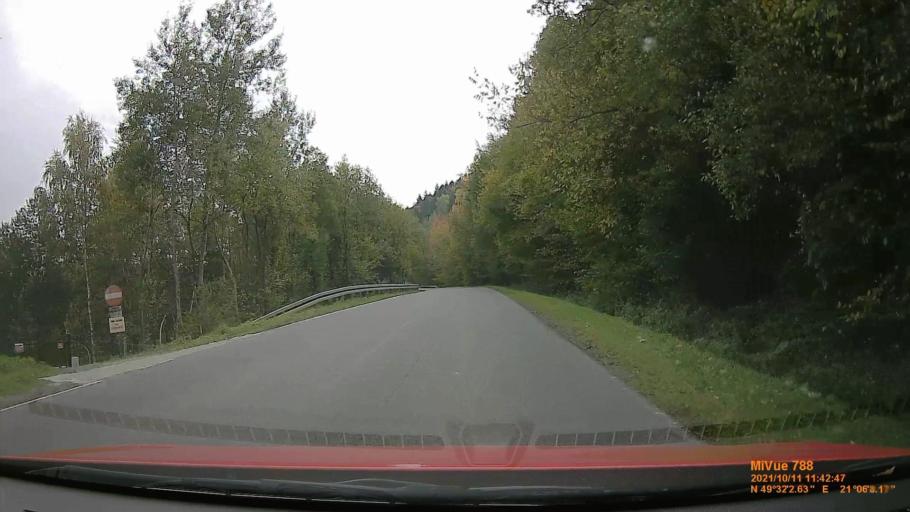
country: PL
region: Lesser Poland Voivodeship
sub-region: Powiat gorlicki
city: Uscie Gorlickie
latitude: 49.5339
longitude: 21.1024
